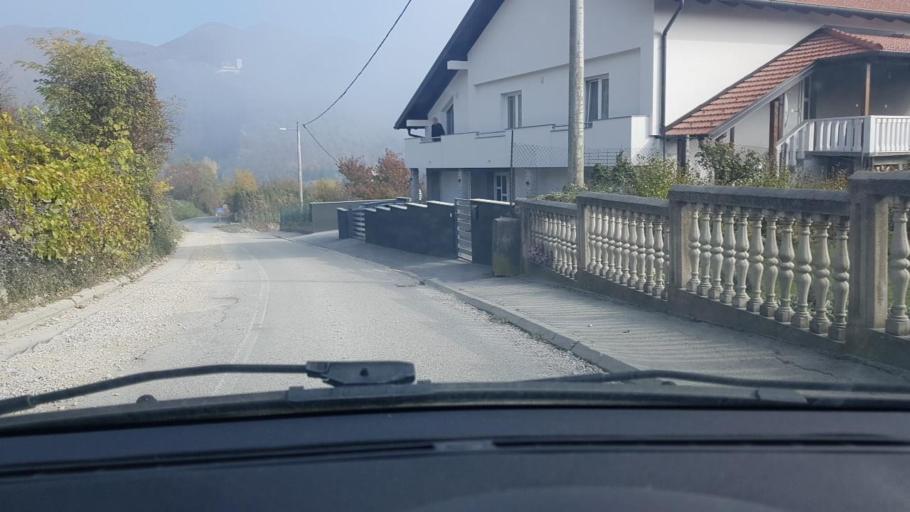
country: HR
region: Krapinsko-Zagorska
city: Zlatar
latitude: 46.1498
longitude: 16.0617
